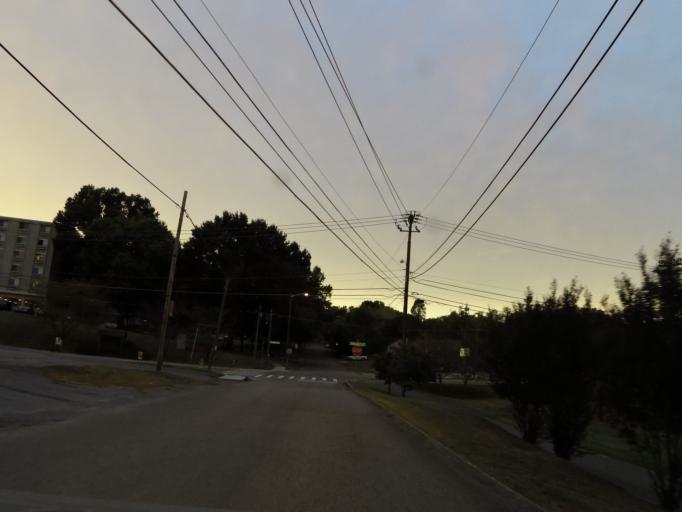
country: US
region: Tennessee
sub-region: Knox County
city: Knoxville
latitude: 35.9449
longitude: -83.9817
